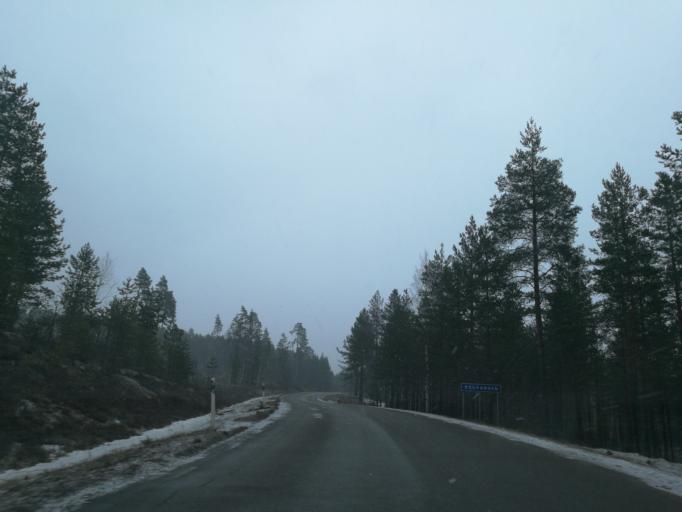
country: NO
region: Hedmark
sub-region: Grue
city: Kirkenaer
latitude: 60.6998
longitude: 12.5710
